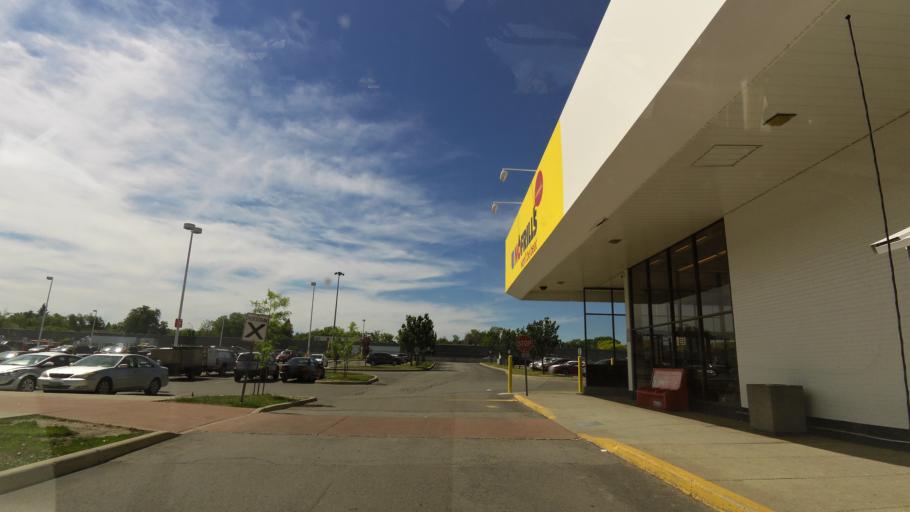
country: CA
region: Ontario
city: Oakville
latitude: 43.4557
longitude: -79.6876
